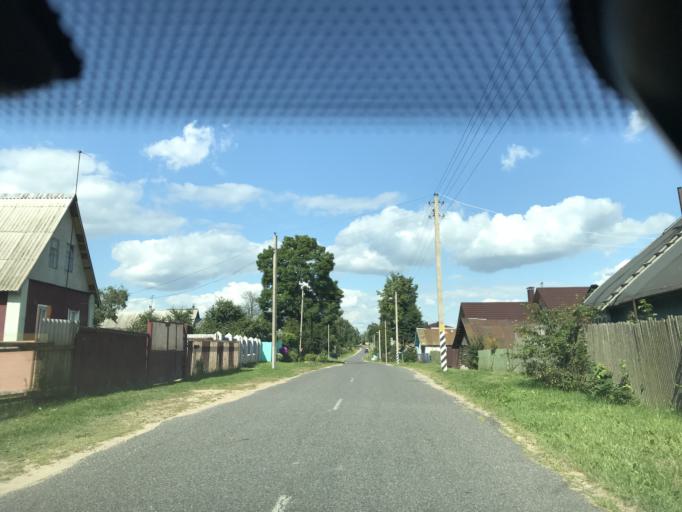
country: BY
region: Mogilev
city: Poselok Voskhod
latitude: 53.7870
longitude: 30.3555
